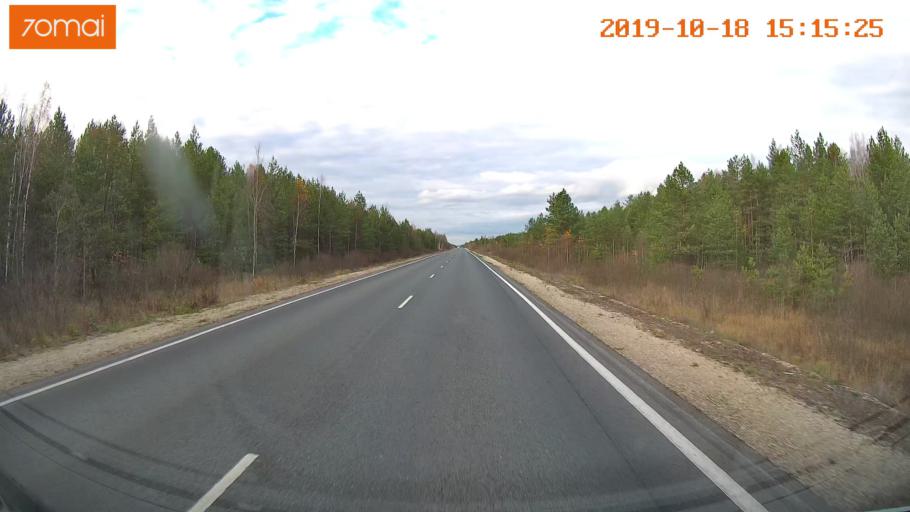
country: RU
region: Vladimir
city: Gus'-Khrustal'nyy
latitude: 55.6186
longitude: 40.7224
